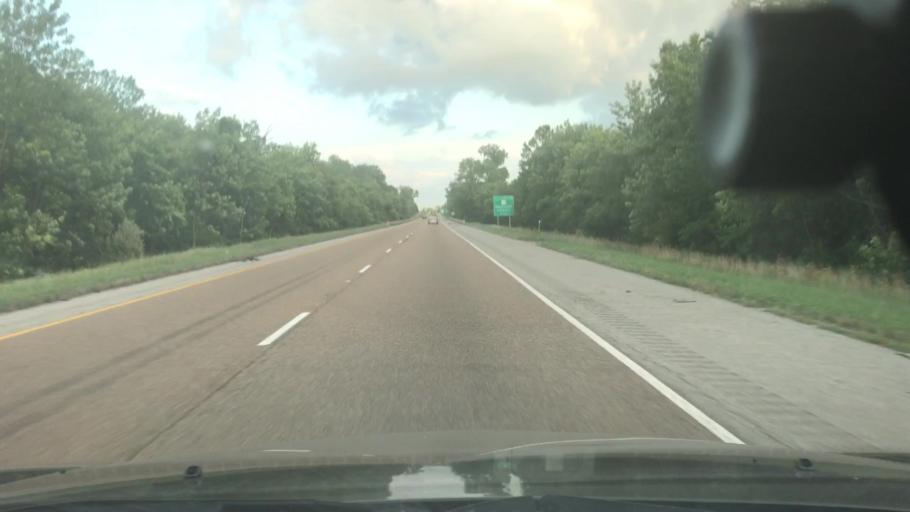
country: US
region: Illinois
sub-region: Saint Clair County
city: Scott Air Force Base
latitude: 38.5602
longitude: -89.8302
